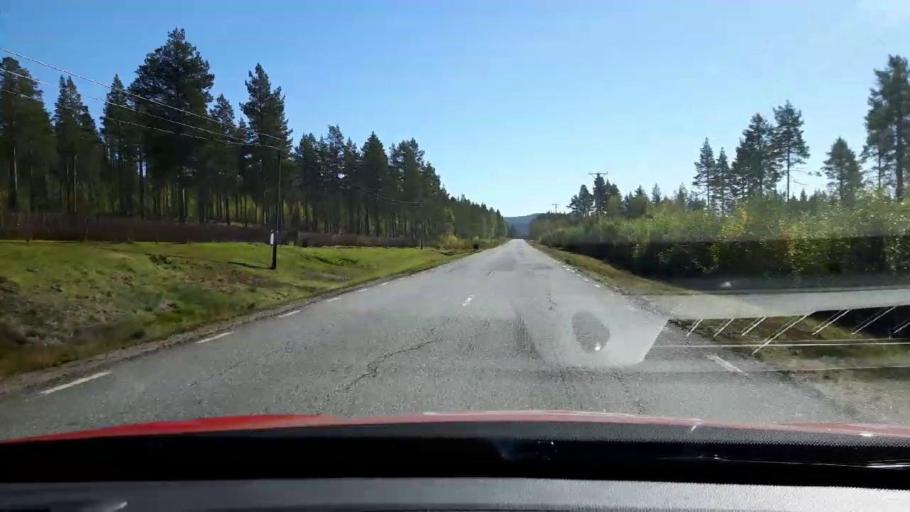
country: SE
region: Jaemtland
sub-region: Harjedalens Kommun
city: Sveg
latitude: 62.3011
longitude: 14.0631
